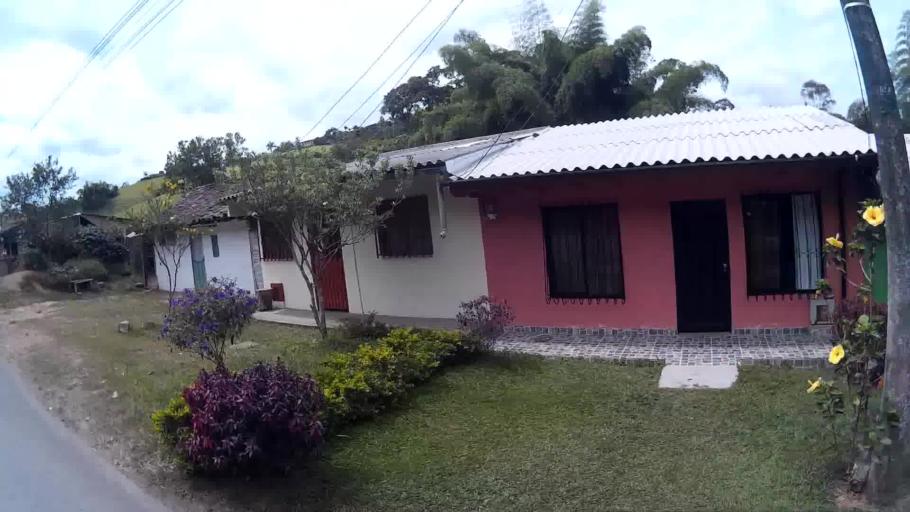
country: CO
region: Risaralda
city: Marsella
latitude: 4.9314
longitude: -75.7416
